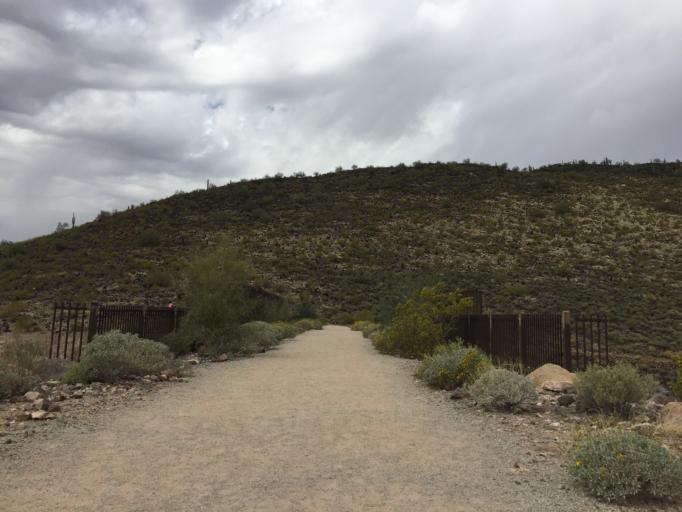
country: US
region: Arizona
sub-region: Maricopa County
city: Peoria
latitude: 33.6924
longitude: -112.1843
